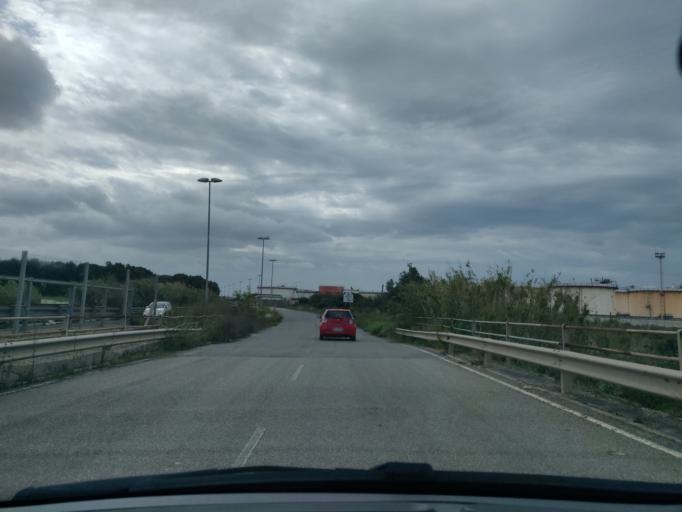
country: IT
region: Latium
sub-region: Citta metropolitana di Roma Capitale
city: Aurelia
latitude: 42.1143
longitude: 11.7796
